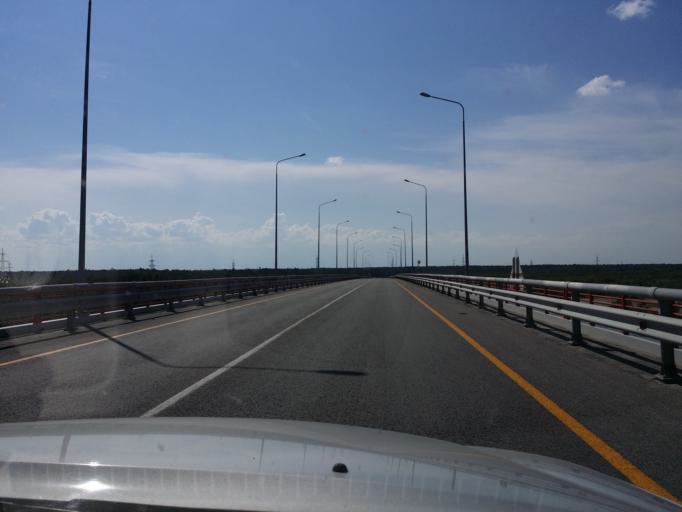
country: RU
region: Khanty-Mansiyskiy Avtonomnyy Okrug
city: Izluchinsk
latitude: 60.9352
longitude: 76.8888
